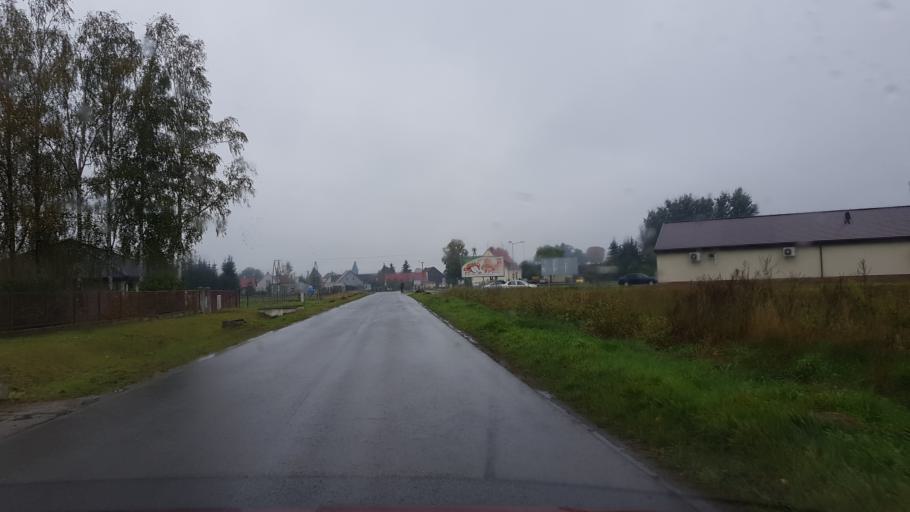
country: PL
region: Greater Poland Voivodeship
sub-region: Powiat zlotowski
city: Tarnowka
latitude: 53.3408
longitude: 16.8617
